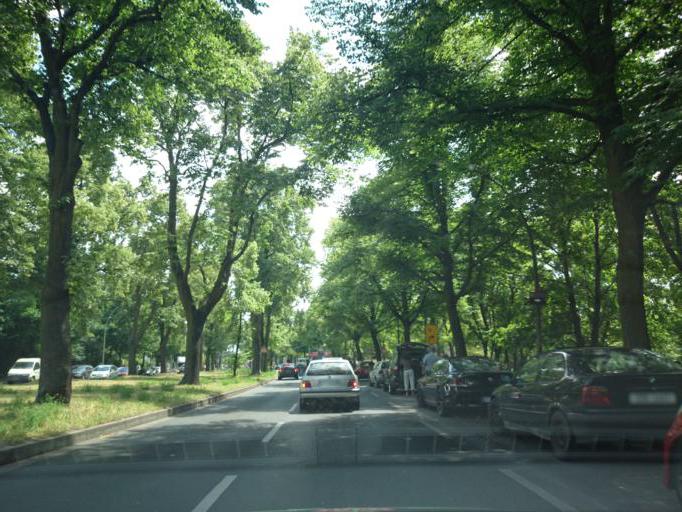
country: DE
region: Berlin
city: Lichtenrade
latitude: 52.3895
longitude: 13.4074
